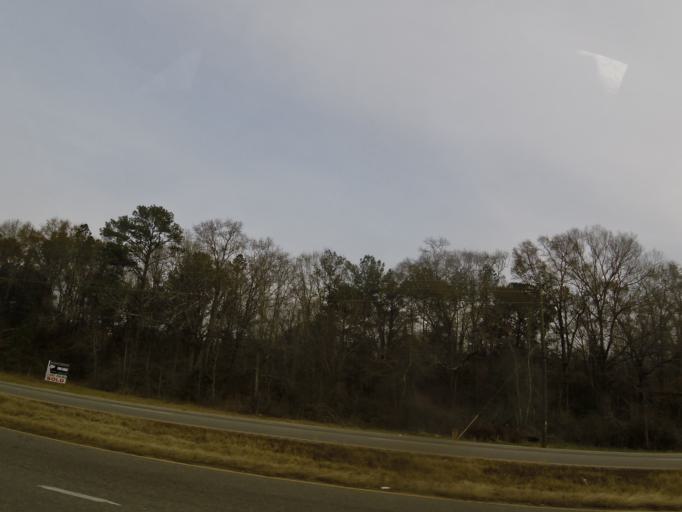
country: US
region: Alabama
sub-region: Montgomery County
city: Pike Road
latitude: 32.2975
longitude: -86.1980
